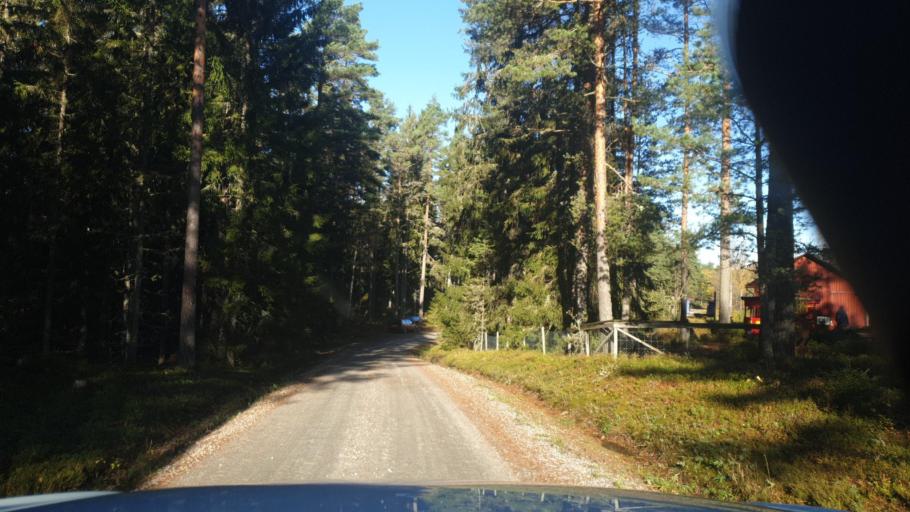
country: SE
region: Vaermland
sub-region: Arvika Kommun
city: Arvika
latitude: 59.5687
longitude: 12.7399
